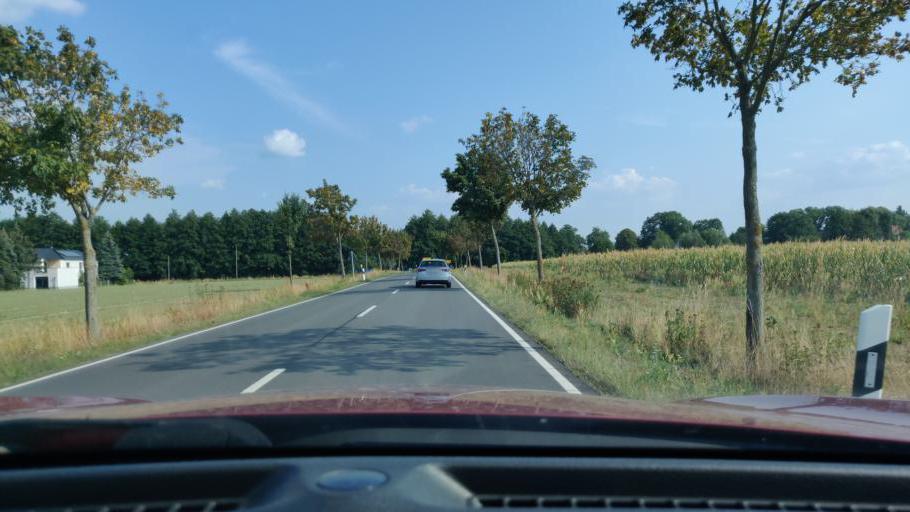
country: DE
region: Saxony
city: Mockrehna
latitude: 51.4942
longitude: 12.8265
